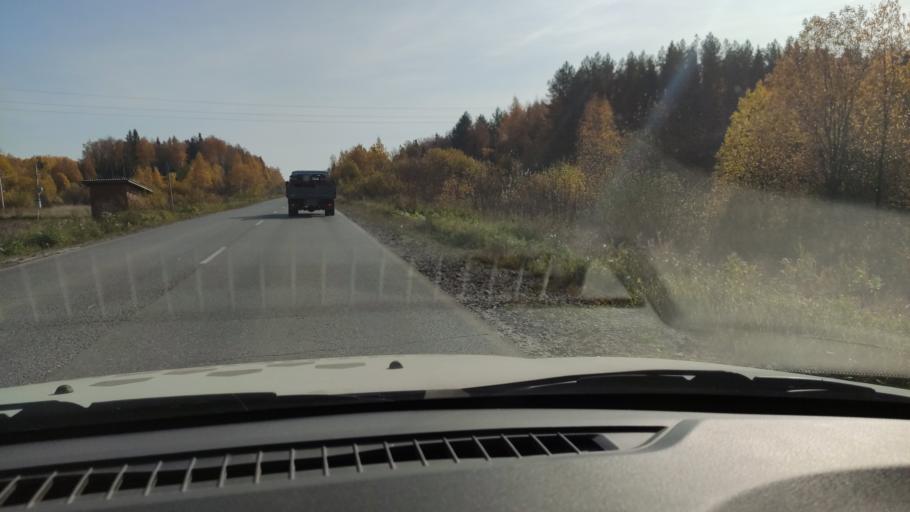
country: RU
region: Perm
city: Novyye Lyady
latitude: 58.0319
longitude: 56.6145
